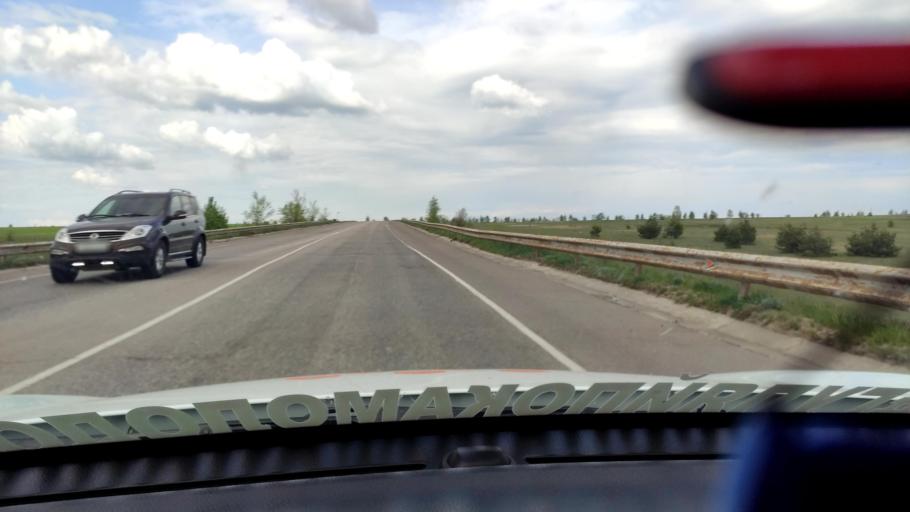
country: RU
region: Voronezj
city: Kolodeznyy
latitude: 51.3880
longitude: 39.2258
